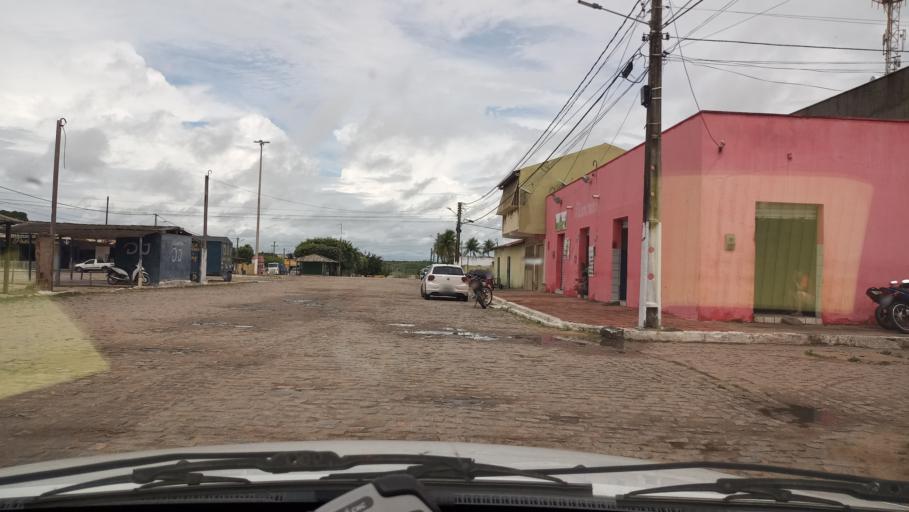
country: BR
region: Rio Grande do Norte
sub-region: Poco Branco
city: Poco Branco
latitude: -5.6191
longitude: -35.6569
